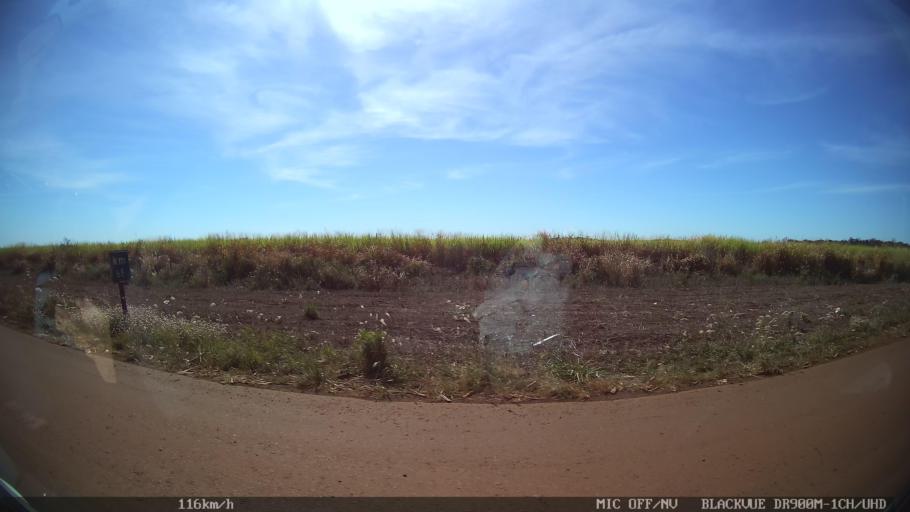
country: BR
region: Sao Paulo
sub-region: Sao Joaquim Da Barra
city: Sao Joaquim da Barra
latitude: -20.5586
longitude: -47.7010
